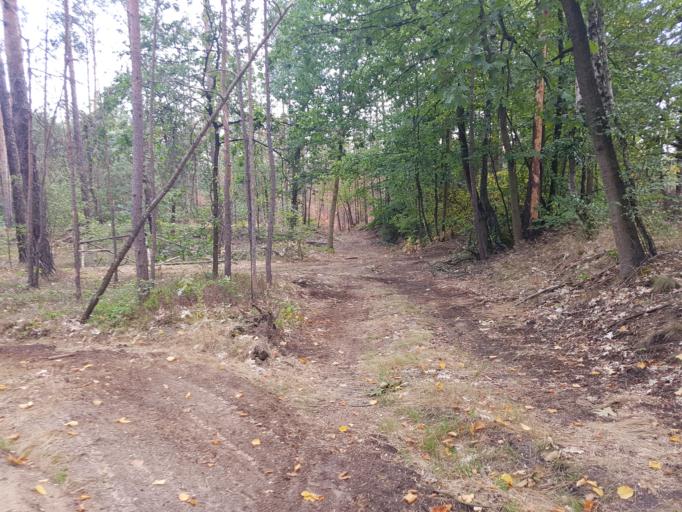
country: DE
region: Brandenburg
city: Finsterwalde
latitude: 51.6310
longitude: 13.6737
